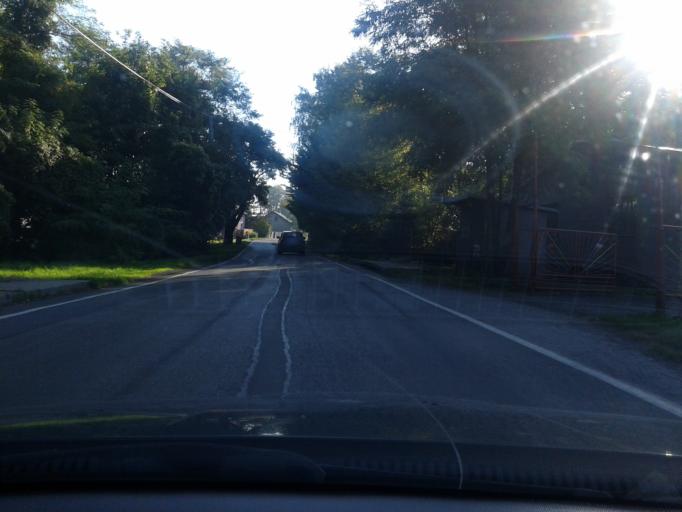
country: CZ
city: Petrvald
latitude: 49.8433
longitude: 18.3990
